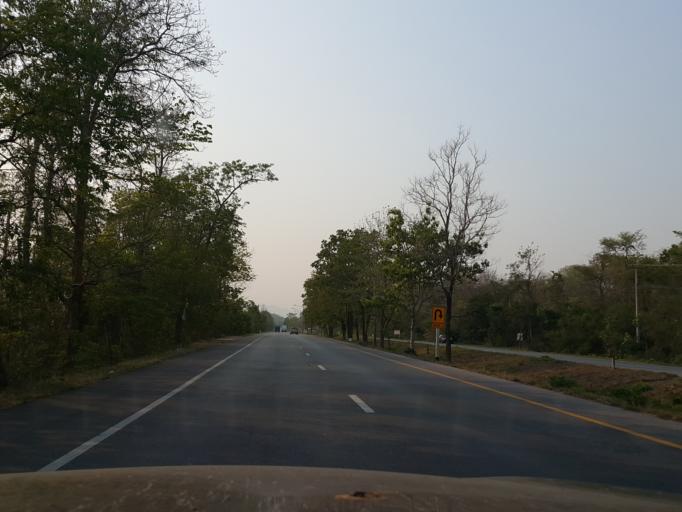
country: TH
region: Lampang
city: Thoen
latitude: 17.6724
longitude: 99.2440
